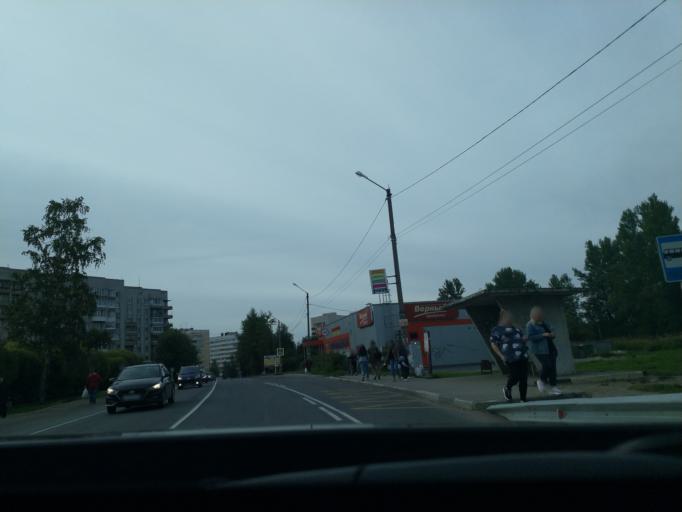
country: RU
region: Leningrad
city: Nikol'skoye
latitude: 59.7082
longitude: 30.7838
